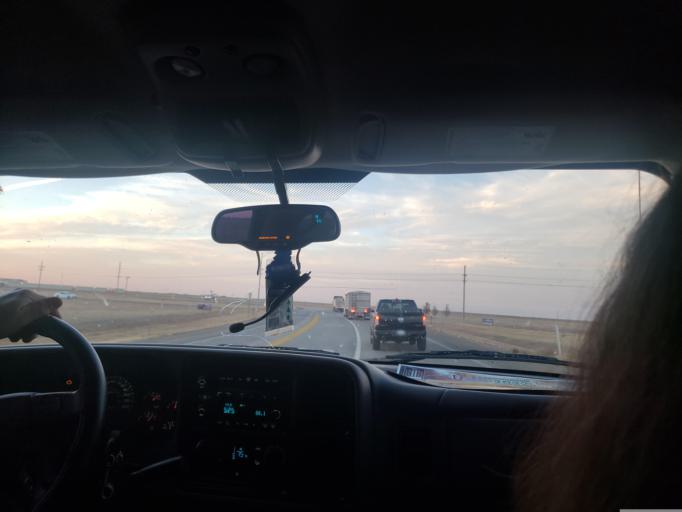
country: US
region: Kansas
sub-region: Seward County
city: Liberal
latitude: 37.0674
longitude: -100.9051
